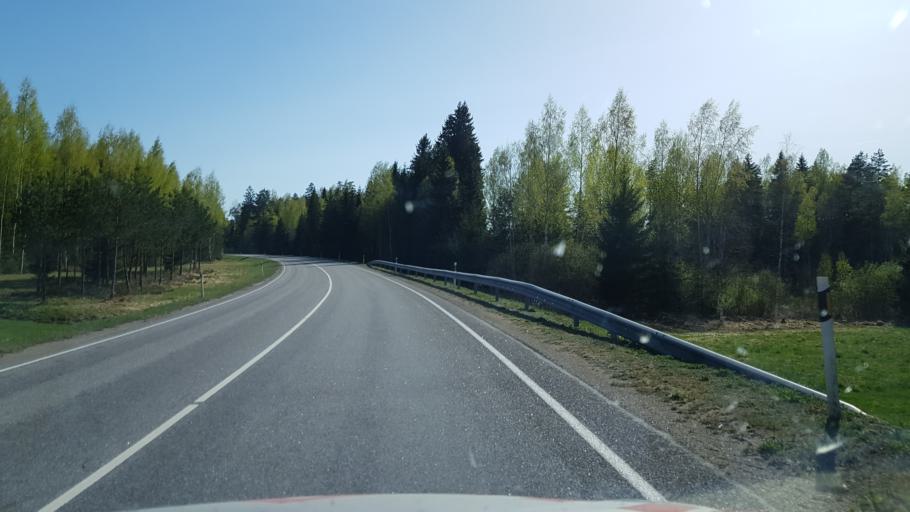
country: EE
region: Paernumaa
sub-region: Saarde vald
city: Kilingi-Nomme
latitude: 58.1915
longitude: 25.0565
